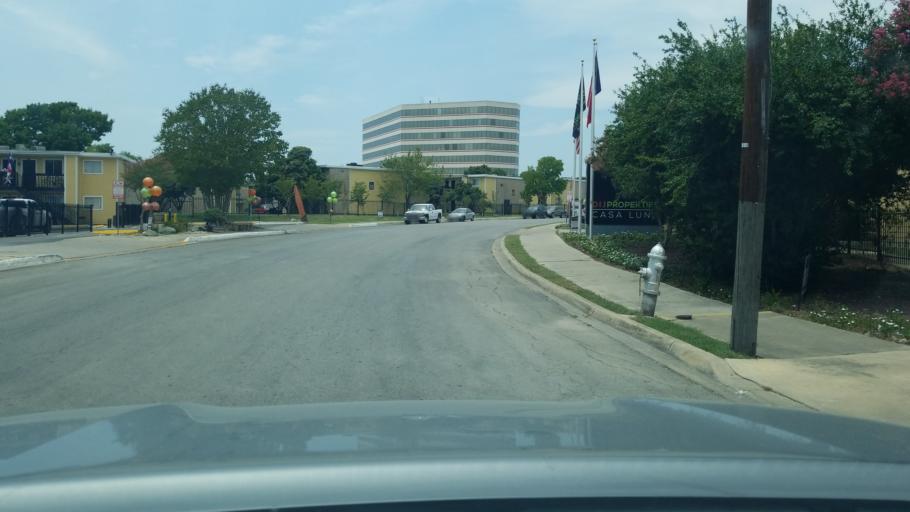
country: US
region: Texas
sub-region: Bexar County
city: Castle Hills
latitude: 29.5312
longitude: -98.4926
